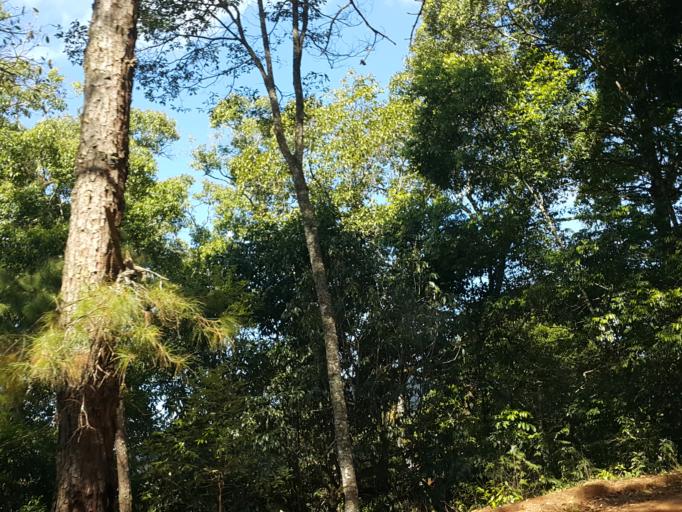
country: TH
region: Chiang Mai
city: Wiang Haeng
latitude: 19.5370
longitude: 98.8139
